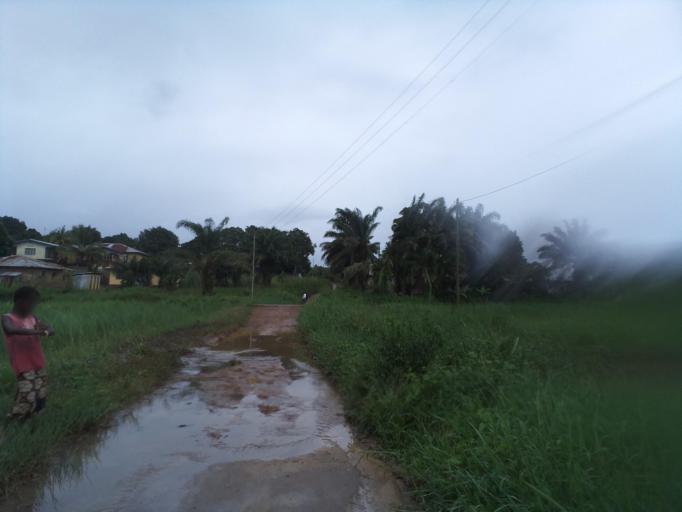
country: SL
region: Eastern Province
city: Kenema
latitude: 7.8498
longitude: -11.1962
